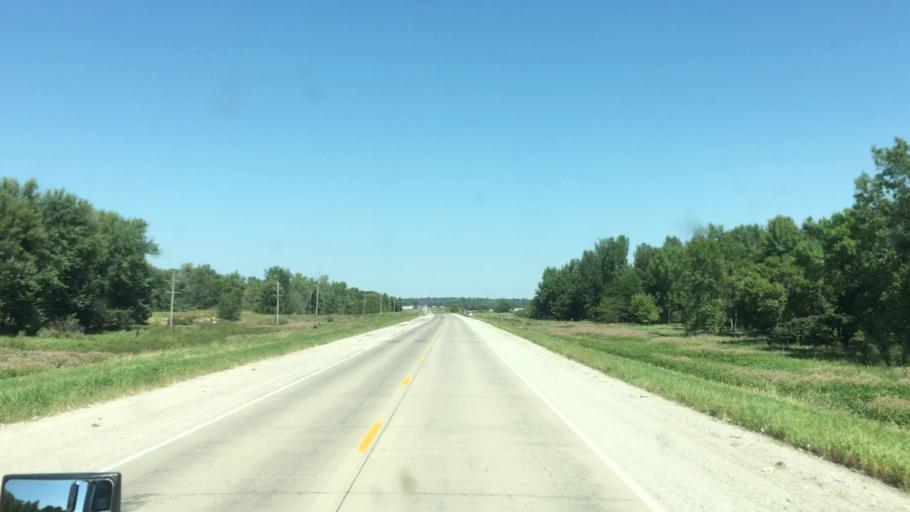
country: US
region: Iowa
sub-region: Benton County
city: Belle Plaine
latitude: 41.8641
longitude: -92.2779
